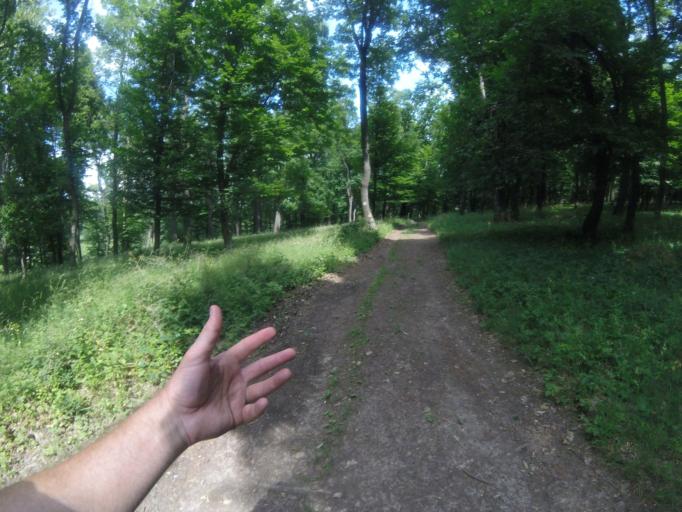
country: HU
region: Fejer
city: Szarliget
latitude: 47.4885
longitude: 18.4609
